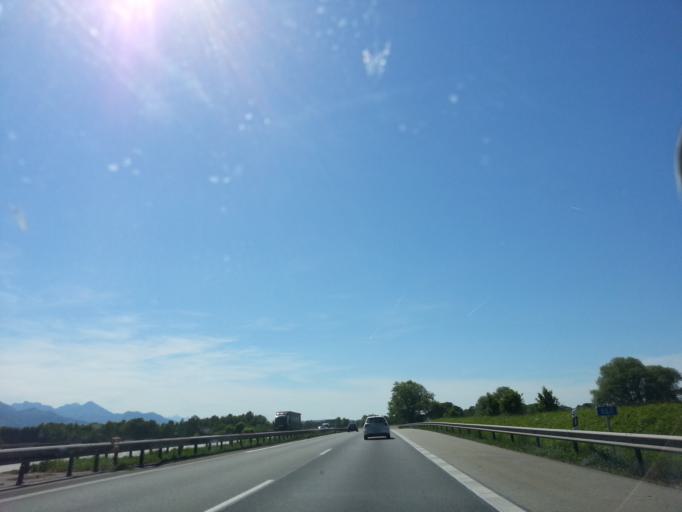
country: DE
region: Bavaria
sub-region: Upper Bavaria
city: Ubersee
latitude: 47.8378
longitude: 12.4561
